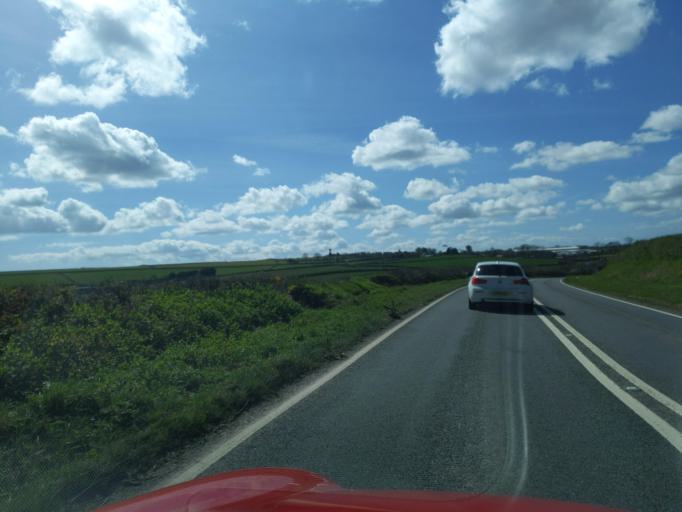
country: GB
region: England
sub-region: Cornwall
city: Liskeard
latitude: 50.4507
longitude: -4.5454
